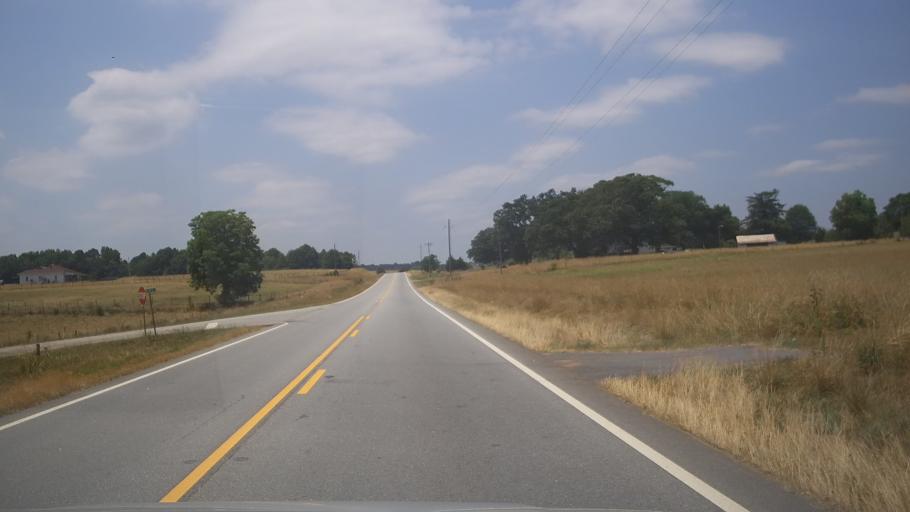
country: US
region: Georgia
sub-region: Madison County
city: Danielsville
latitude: 34.1805
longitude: -83.3276
